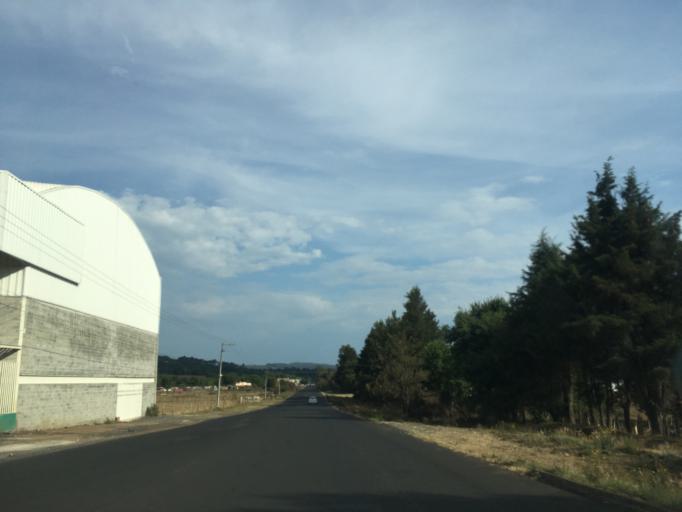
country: MX
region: Michoacan
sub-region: Tingueindin
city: Tingueindin
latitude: 19.7789
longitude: -102.5045
